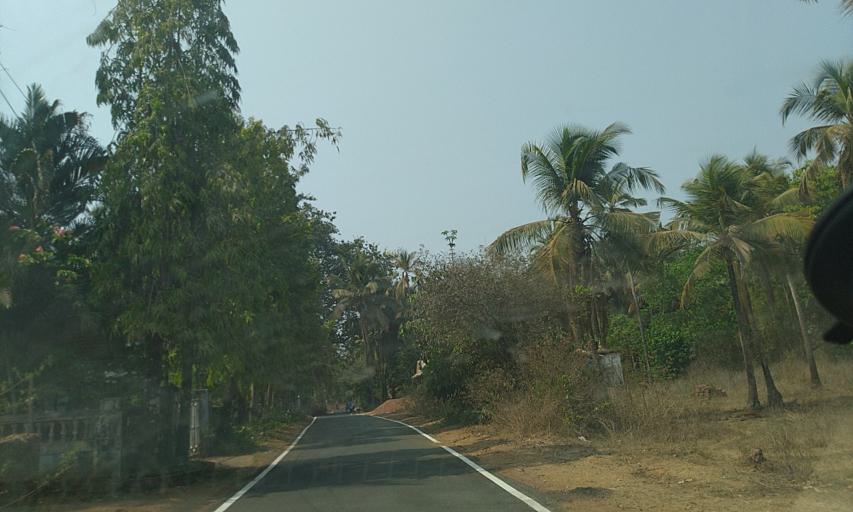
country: IN
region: Goa
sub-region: South Goa
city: Raia
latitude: 15.3019
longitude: 73.9463
